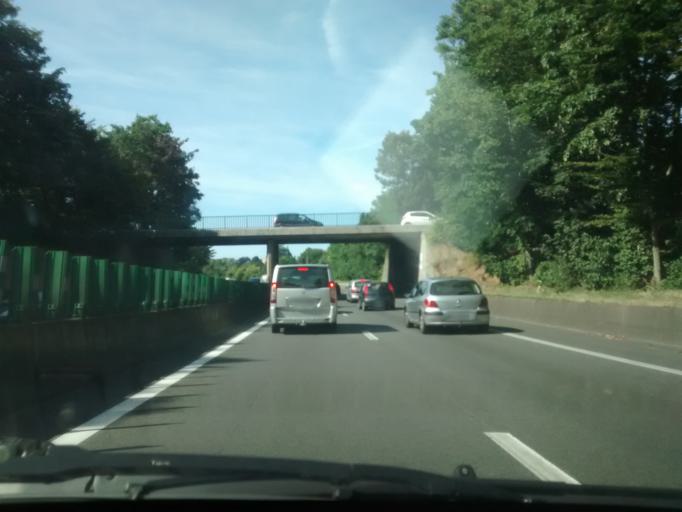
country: FR
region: Brittany
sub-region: Departement des Cotes-d'Armor
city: Saint-Brieuc
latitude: 48.5136
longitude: -2.7427
